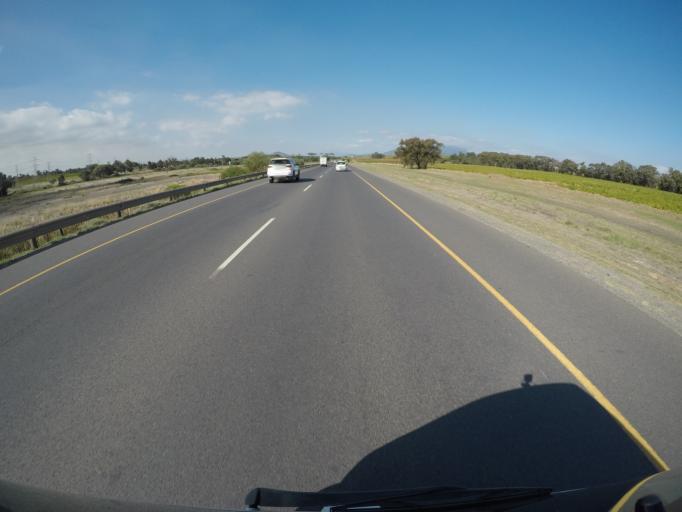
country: ZA
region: Western Cape
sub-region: City of Cape Town
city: Kraaifontein
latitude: -33.8826
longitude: 18.7562
